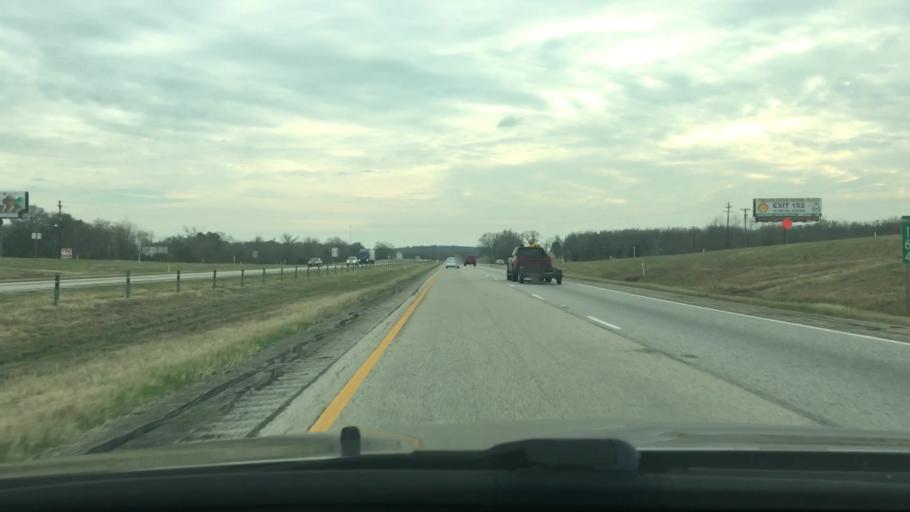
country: US
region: Texas
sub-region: Leon County
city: Centerville
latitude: 31.2570
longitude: -95.9882
